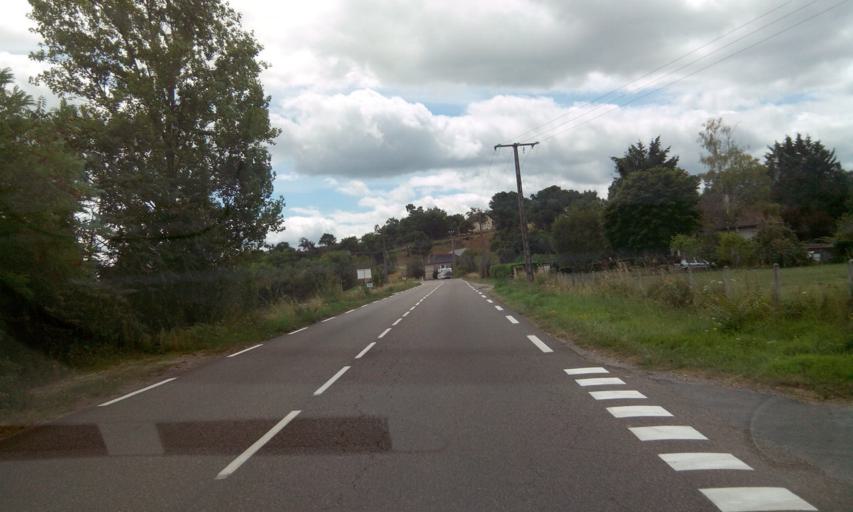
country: FR
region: Limousin
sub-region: Departement de la Correze
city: Brive-la-Gaillarde
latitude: 45.1339
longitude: 1.5522
